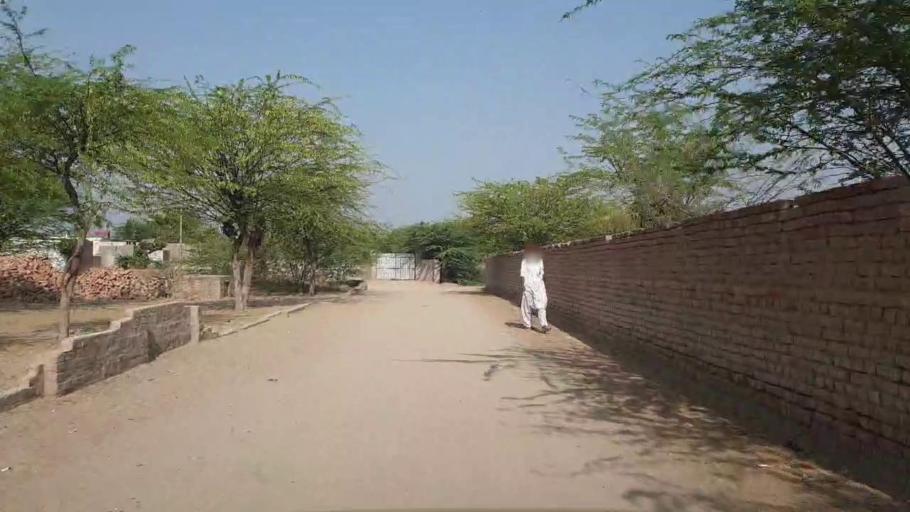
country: PK
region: Sindh
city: Umarkot
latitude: 25.3362
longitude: 69.7388
